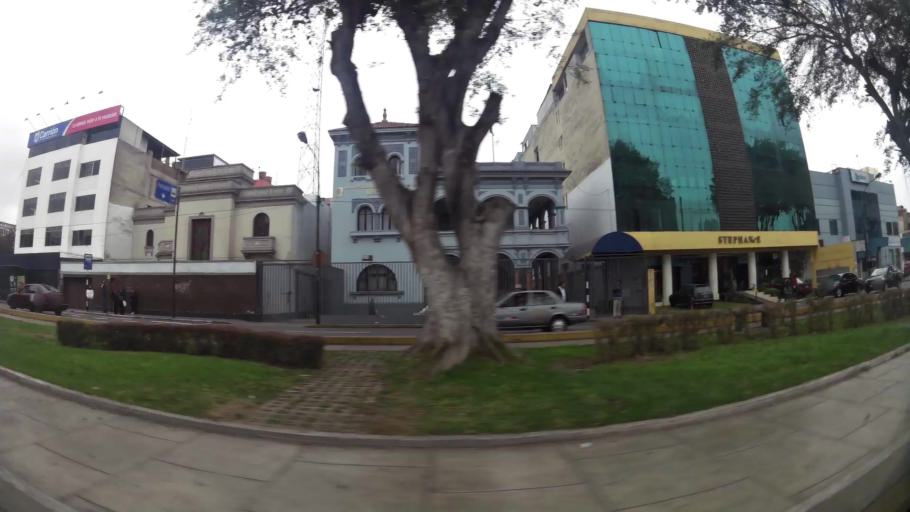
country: PE
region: Lima
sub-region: Lima
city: San Isidro
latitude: -12.0830
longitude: -77.0347
